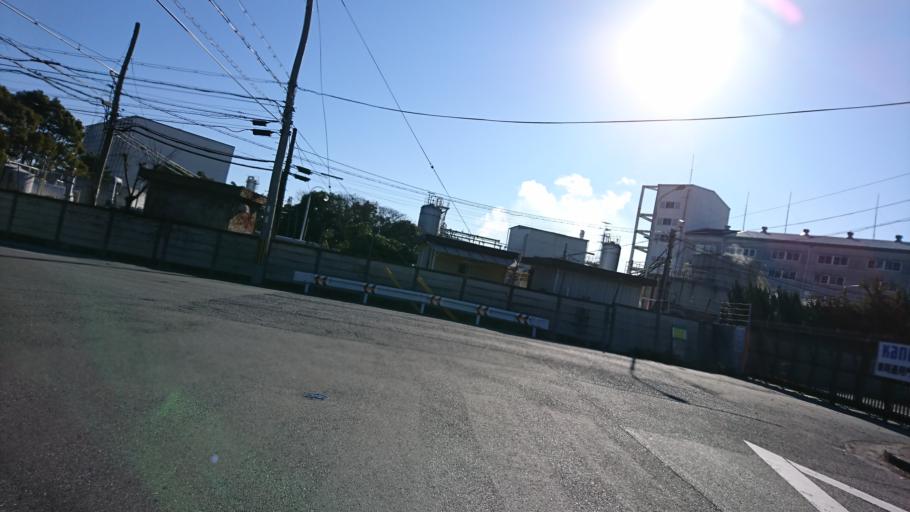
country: JP
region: Hyogo
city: Kakogawacho-honmachi
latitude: 34.7424
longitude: 134.7973
